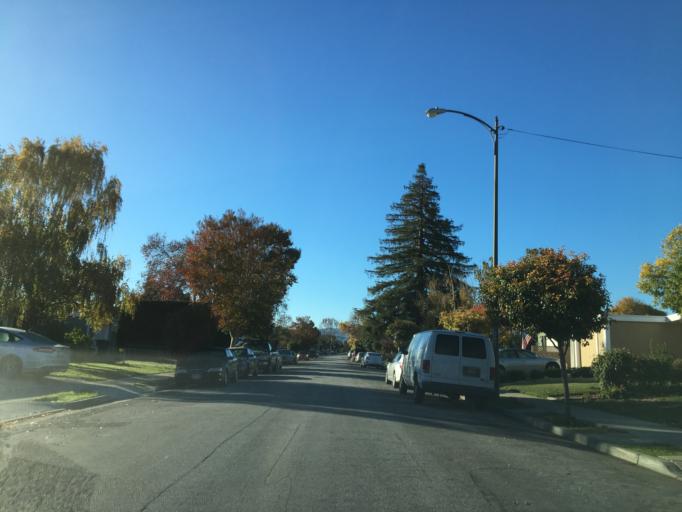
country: US
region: California
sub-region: Santa Clara County
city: Sunnyvale
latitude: 37.3962
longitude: -122.0242
